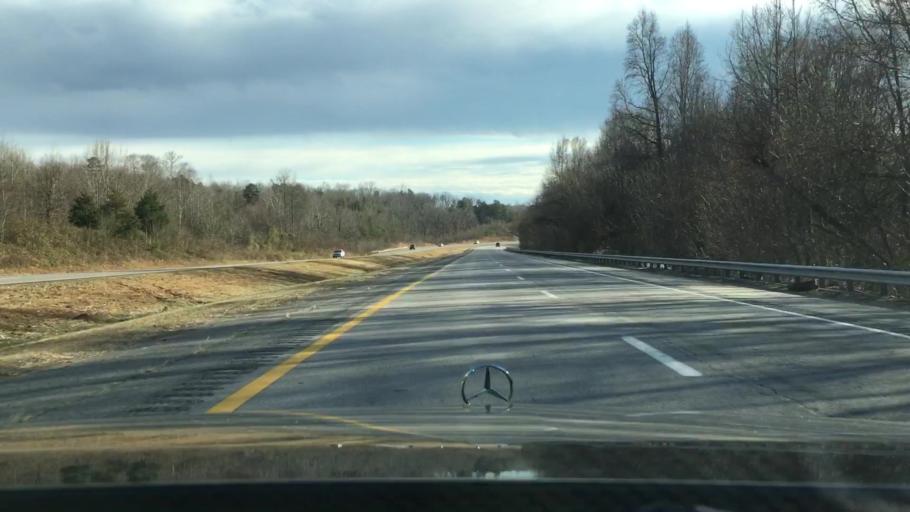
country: US
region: Virginia
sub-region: City of Danville
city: Danville
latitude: 36.6071
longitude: -79.3580
